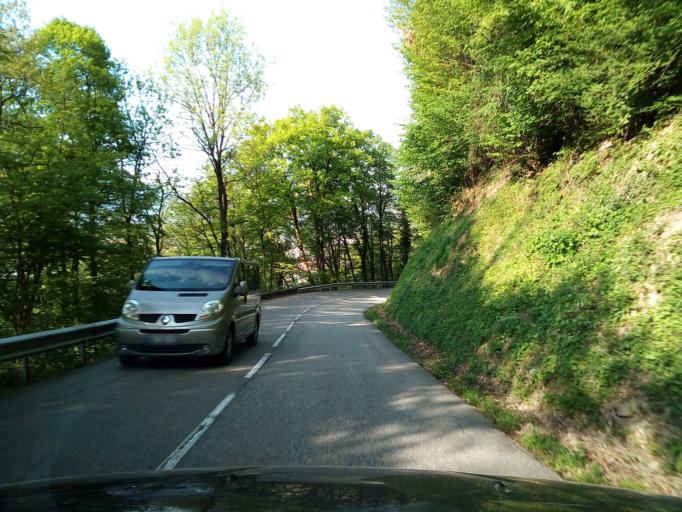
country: FR
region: Rhone-Alpes
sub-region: Departement de l'Isere
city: Domene
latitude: 45.2022
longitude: 5.8471
